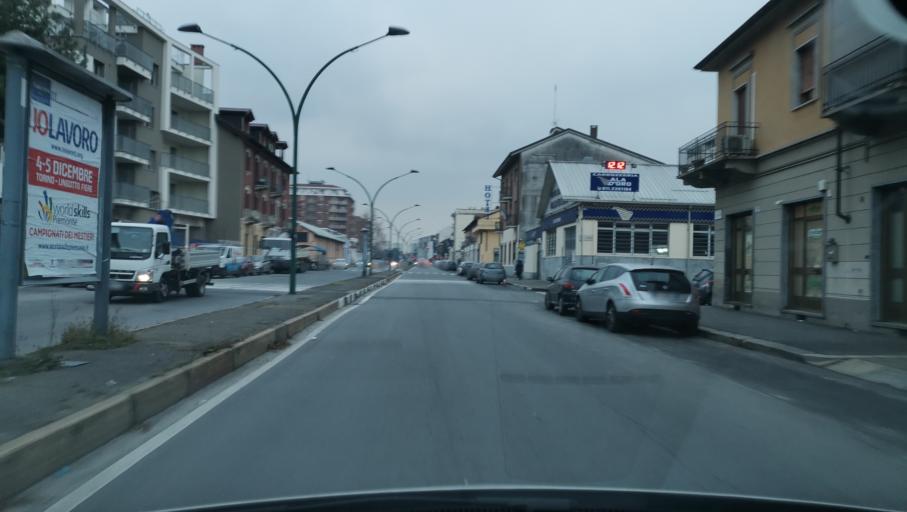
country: IT
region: Piedmont
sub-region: Provincia di Torino
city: Turin
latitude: 45.1064
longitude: 7.6849
